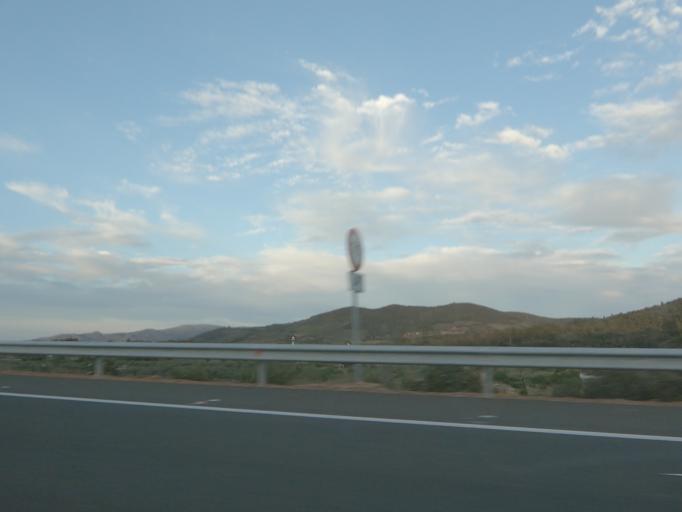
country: ES
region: Extremadura
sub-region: Provincia de Caceres
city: Alcuescar
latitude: 39.1626
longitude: -6.2705
